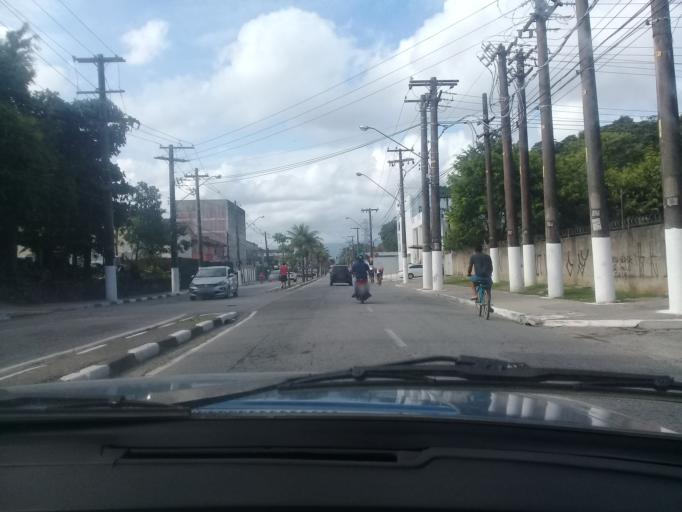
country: BR
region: Sao Paulo
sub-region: Guaruja
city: Guaruja
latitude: -24.0023
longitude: -46.2738
